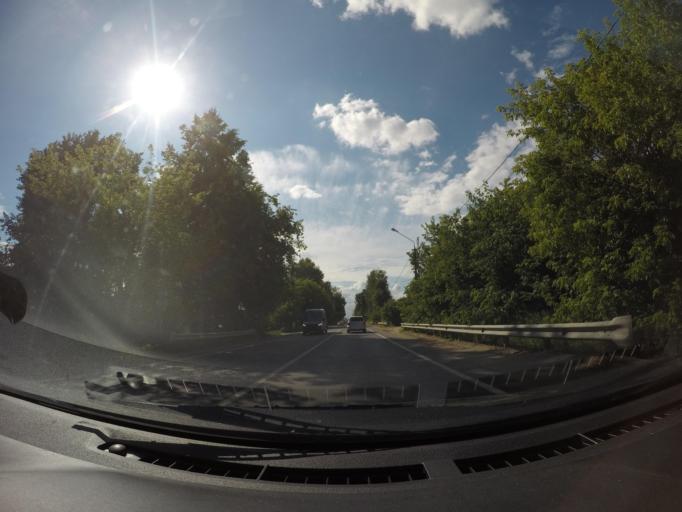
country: RU
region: Moskovskaya
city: Rechitsy
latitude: 55.5897
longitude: 38.5021
